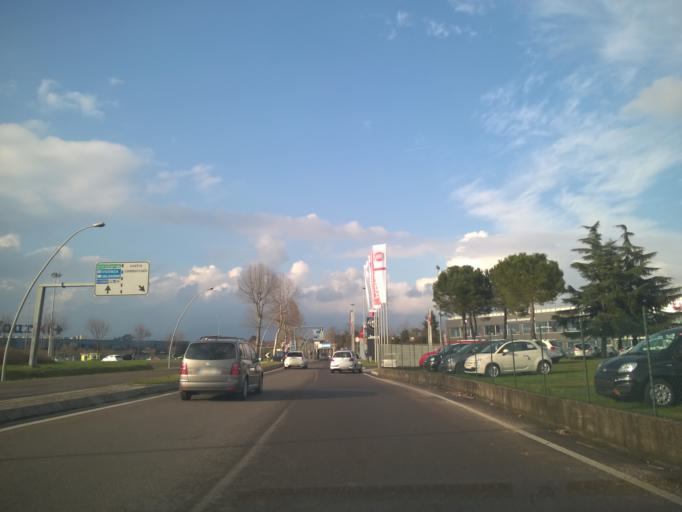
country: IT
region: Veneto
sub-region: Provincia di Vicenza
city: Thiene
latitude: 45.6927
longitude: 11.4831
